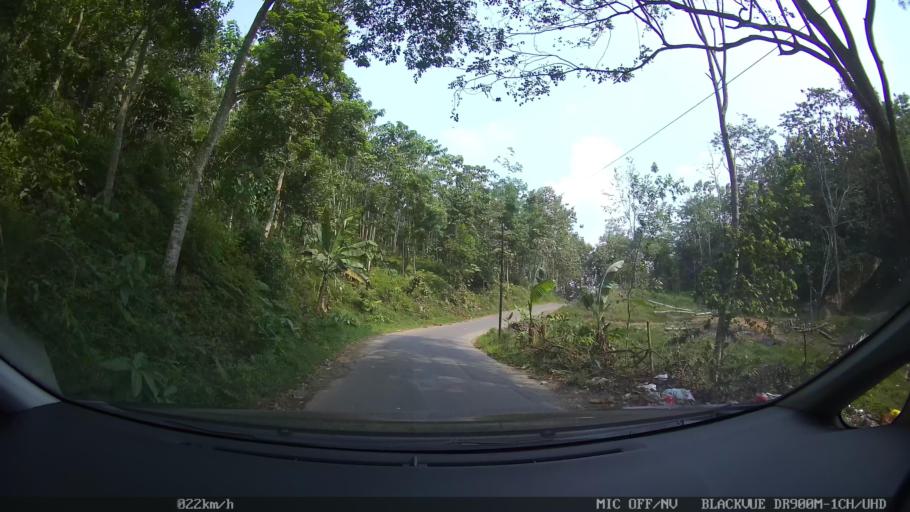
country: ID
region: Lampung
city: Pringsewu
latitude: -5.3860
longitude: 104.9935
